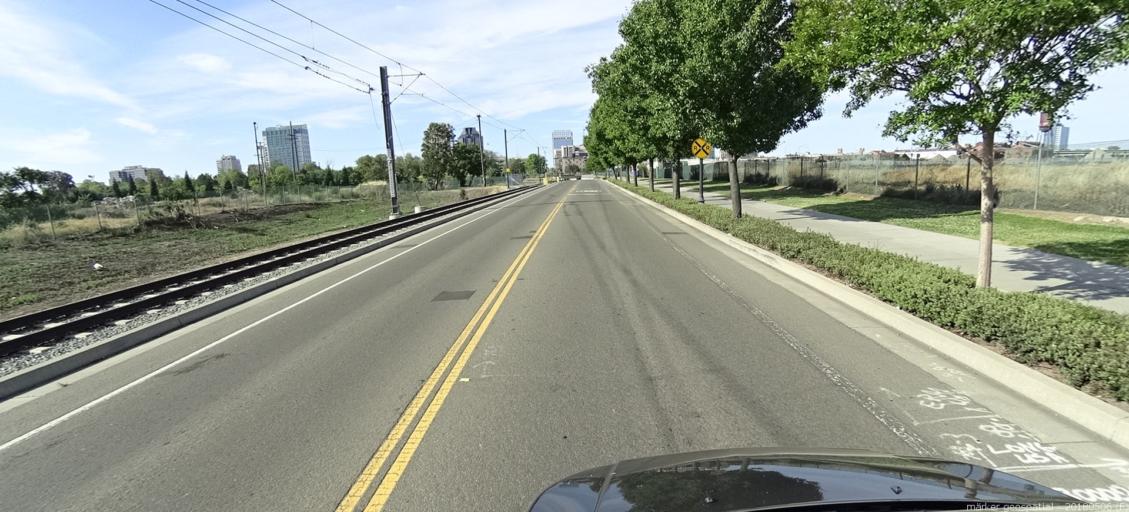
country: US
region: California
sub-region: Sacramento County
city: Sacramento
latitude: 38.5910
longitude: -121.4934
